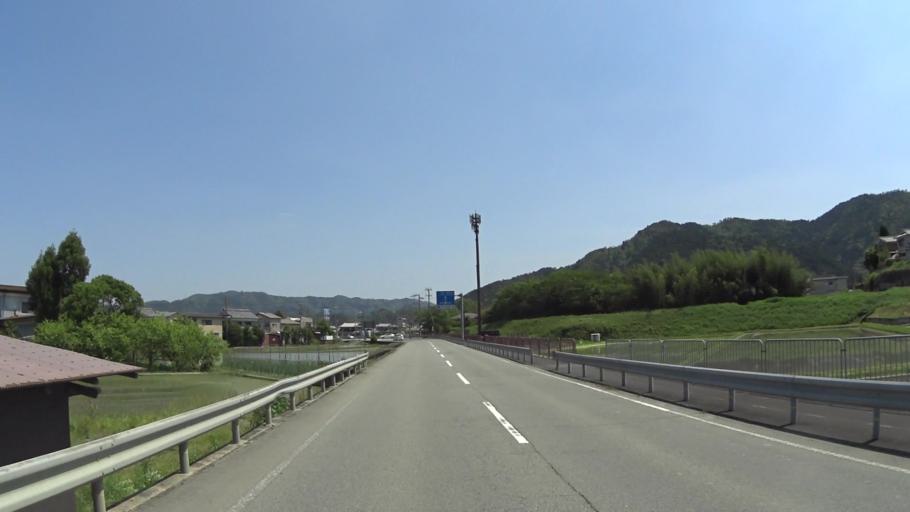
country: JP
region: Kyoto
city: Kameoka
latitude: 35.0194
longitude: 135.5291
